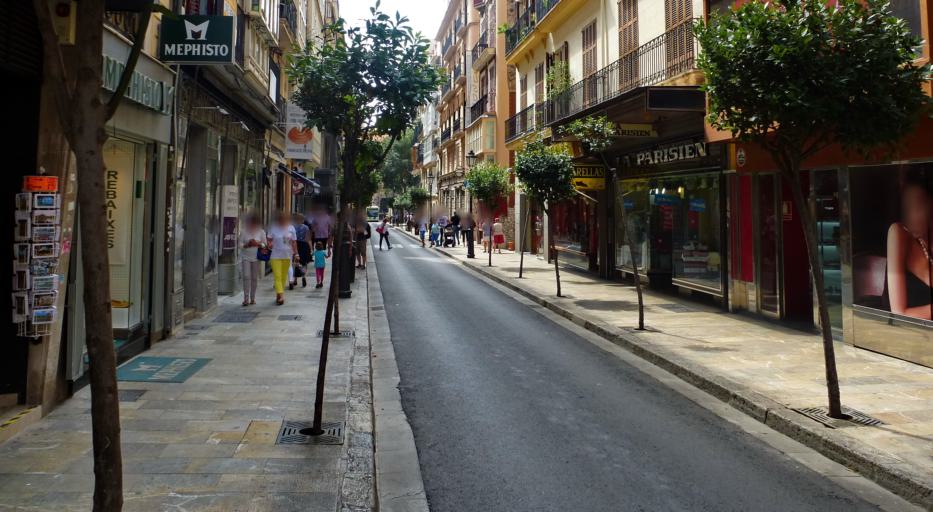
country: ES
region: Balearic Islands
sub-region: Illes Balears
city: Palma
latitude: 39.5705
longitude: 2.6510
